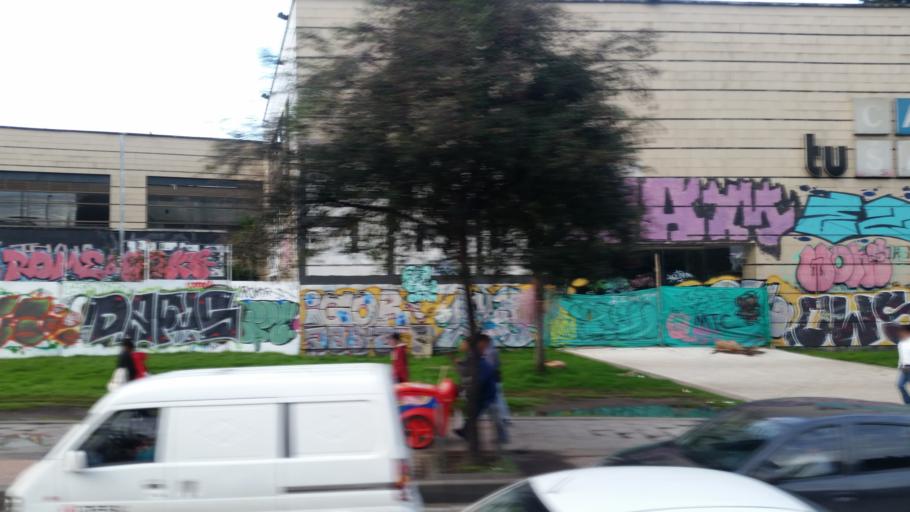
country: CO
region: Cundinamarca
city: Cota
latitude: 4.7431
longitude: -74.0916
